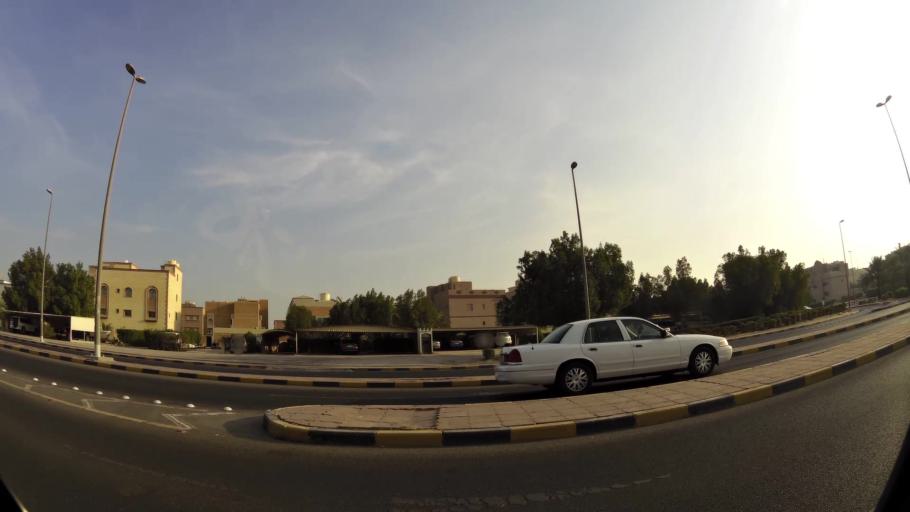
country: KW
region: Mubarak al Kabir
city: Sabah as Salim
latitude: 29.2213
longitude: 48.0623
